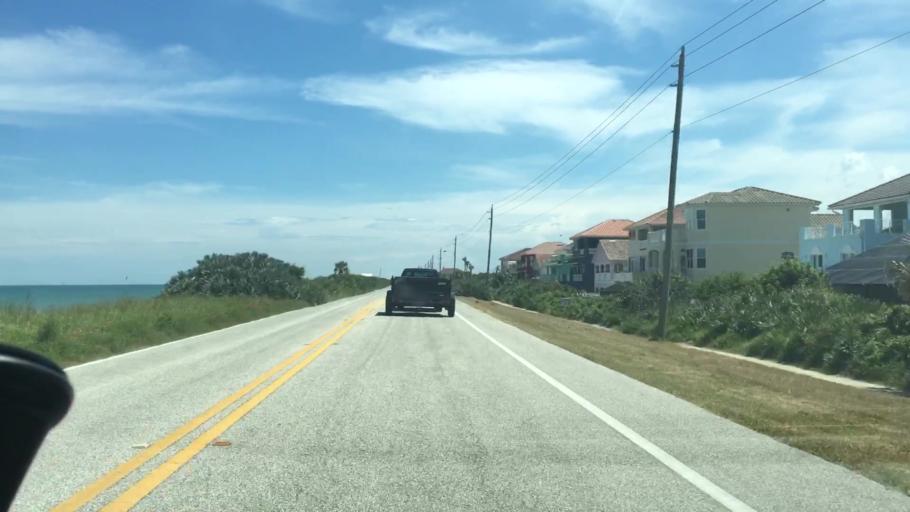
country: US
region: Florida
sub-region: Volusia County
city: Ormond-by-the-Sea
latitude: 29.3885
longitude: -81.0850
